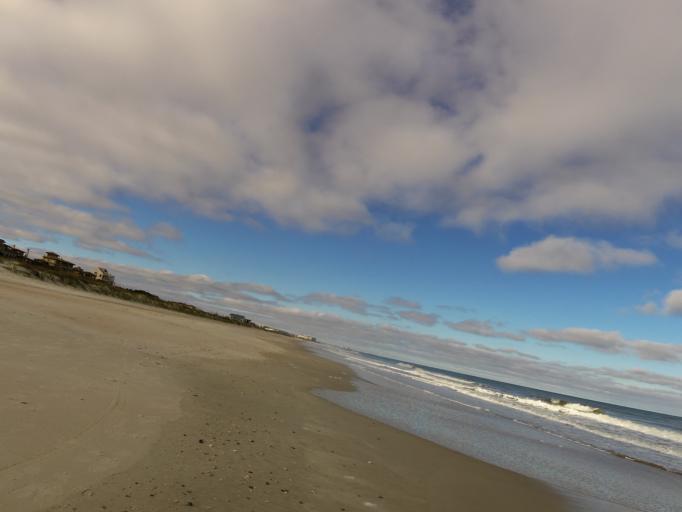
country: US
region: Florida
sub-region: Nassau County
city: Fernandina Beach
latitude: 30.5640
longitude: -81.4426
